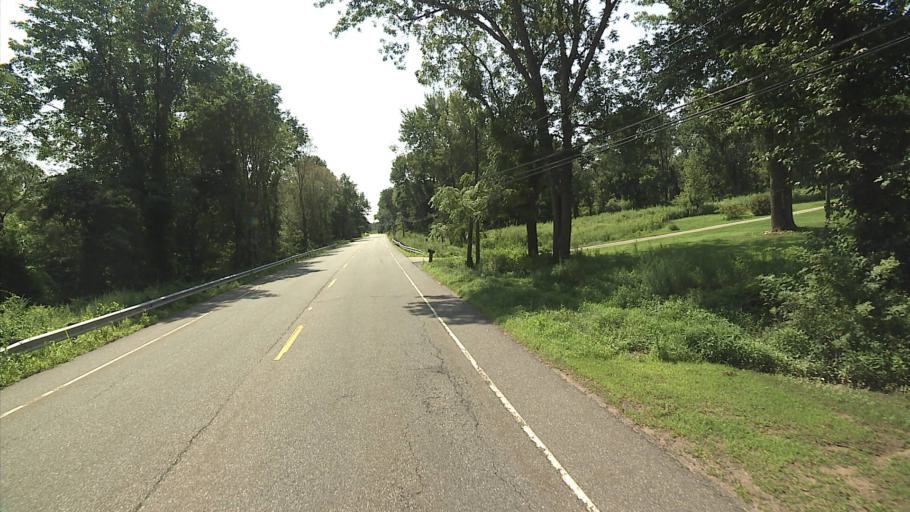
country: US
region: Connecticut
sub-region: New London County
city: Colchester
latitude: 41.5199
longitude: -72.2561
